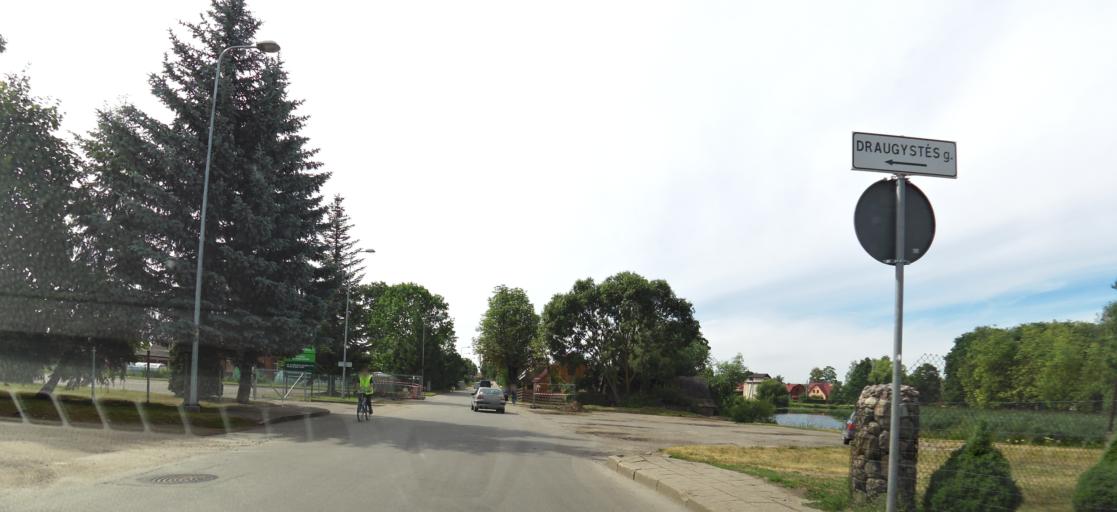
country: LT
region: Panevezys
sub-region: Birzai
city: Birzai
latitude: 56.2046
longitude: 24.7669
